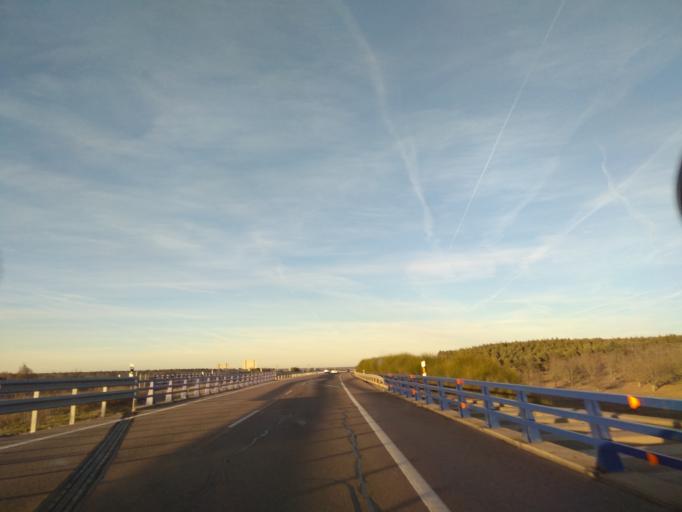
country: ES
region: Castille and Leon
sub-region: Provincia de Salamanca
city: Tenebron
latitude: 40.6792
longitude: -6.4281
